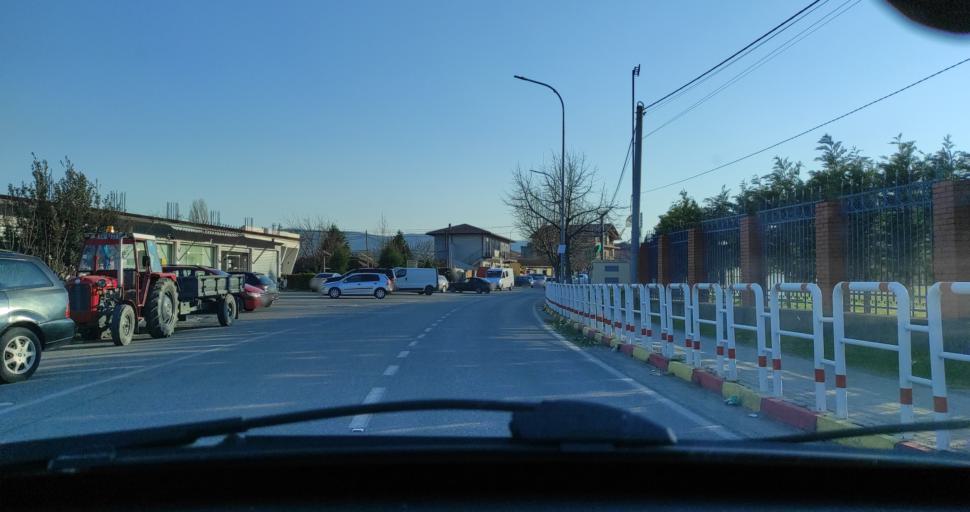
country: AL
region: Shkoder
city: Vukatane
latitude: 41.9605
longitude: 19.5361
